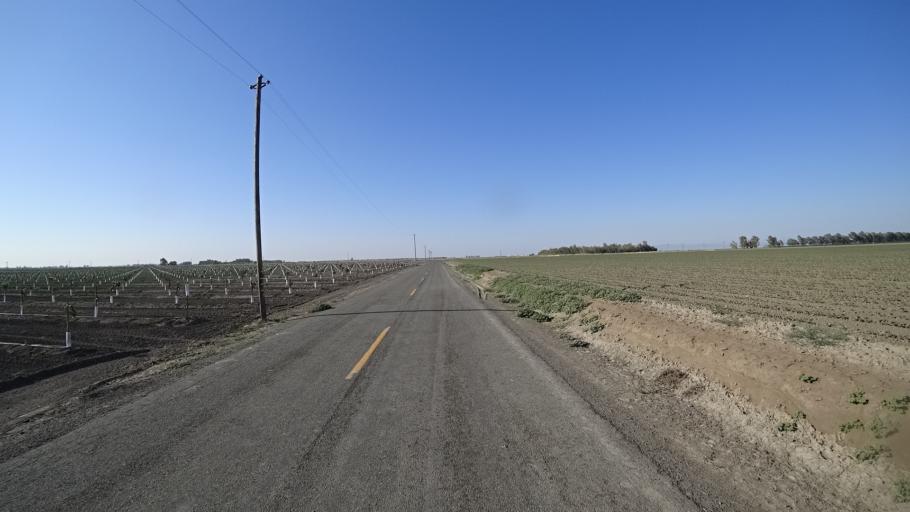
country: US
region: California
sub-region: Fresno County
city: Riverdale
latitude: 36.3830
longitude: -119.9279
